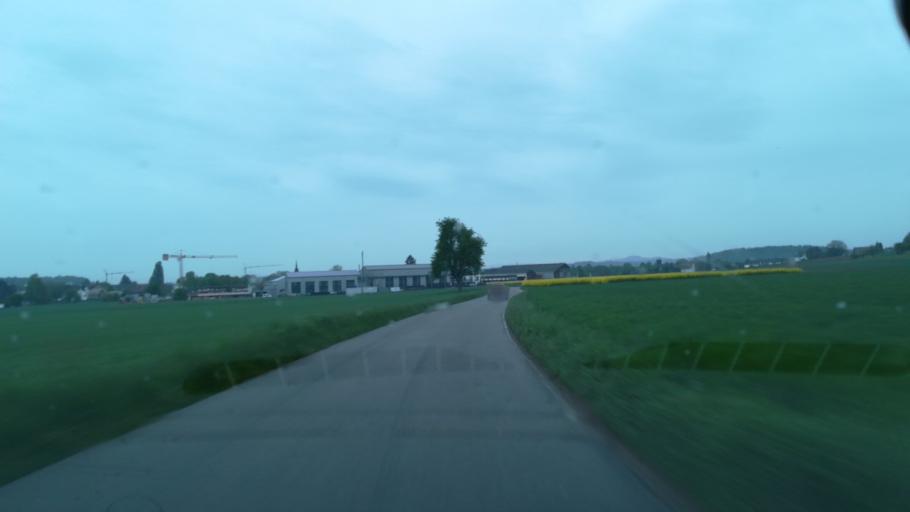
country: CH
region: Zurich
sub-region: Bezirk Buelach
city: End-Hoeri
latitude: 47.5134
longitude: 8.5018
